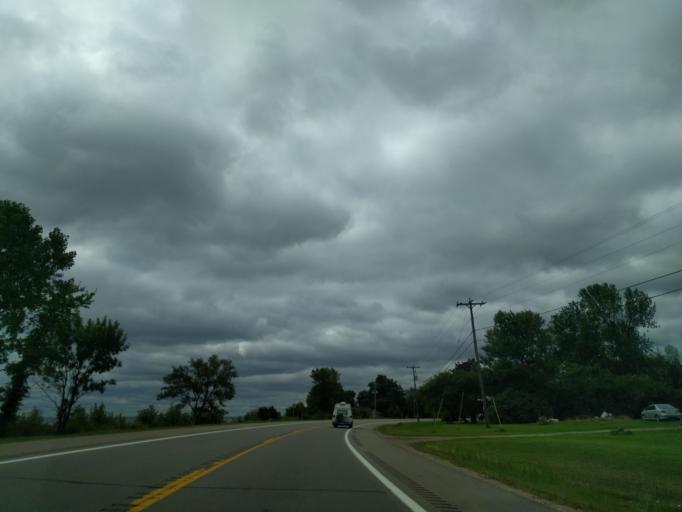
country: US
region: Michigan
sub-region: Menominee County
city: Menominee
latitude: 45.1974
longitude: -87.5382
